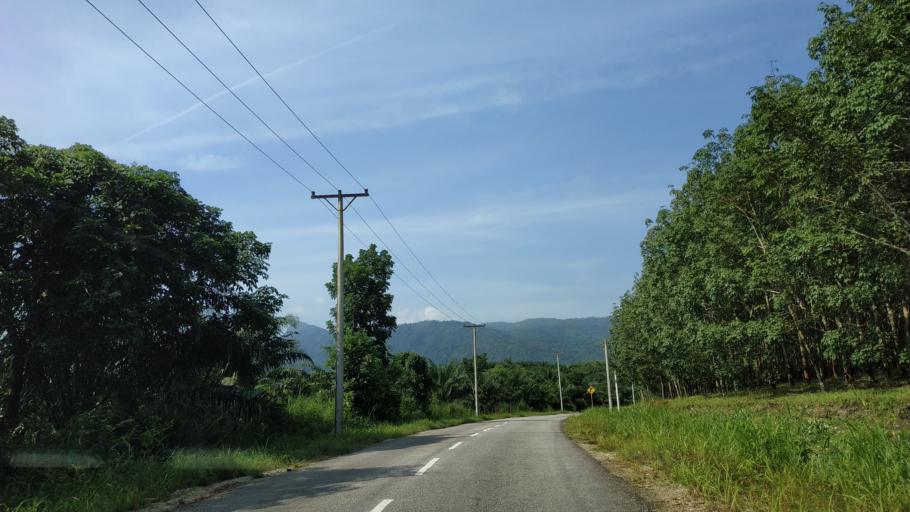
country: MM
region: Tanintharyi
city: Dawei
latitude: 14.5928
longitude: 98.0725
